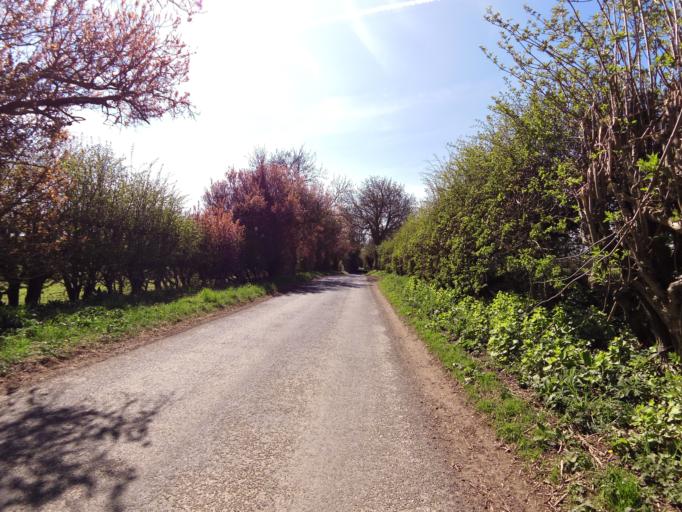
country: GB
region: Scotland
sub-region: Angus
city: Montrose
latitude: 56.6570
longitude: -2.5120
